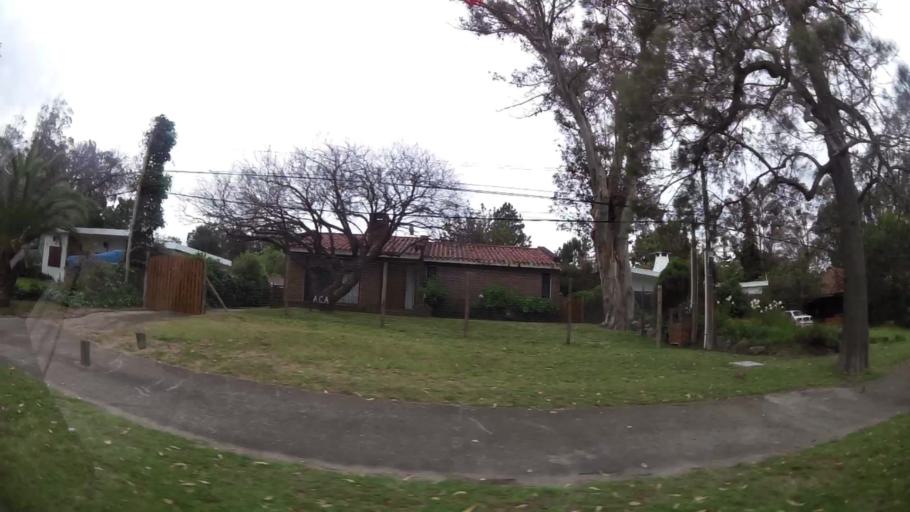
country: UY
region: Maldonado
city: Maldonado
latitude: -34.9078
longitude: -54.9940
